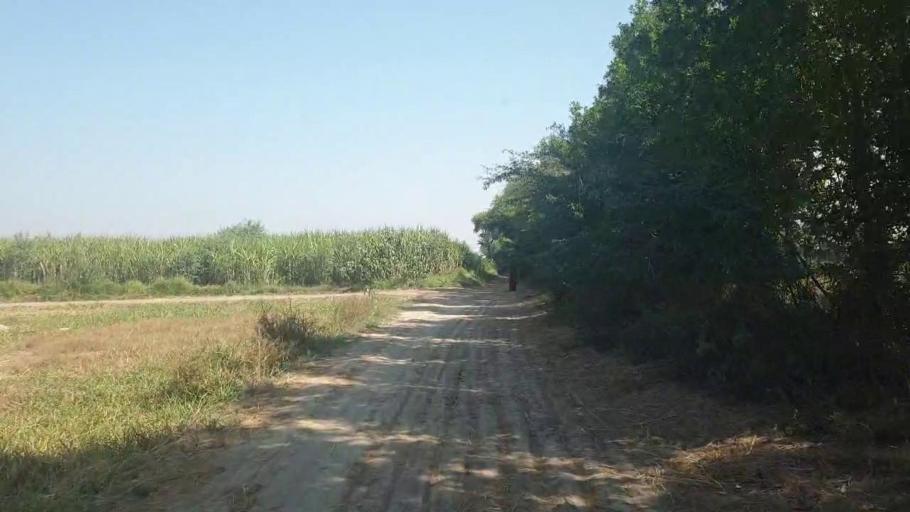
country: PK
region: Sindh
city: Badin
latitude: 24.6822
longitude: 68.8728
